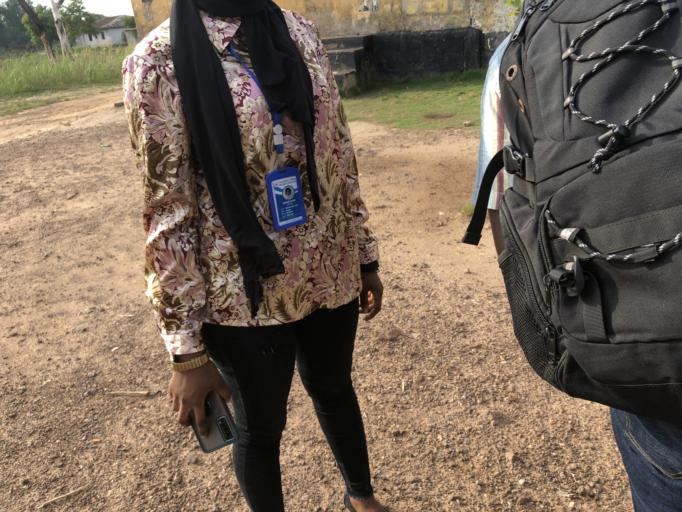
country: SL
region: Northern Province
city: Yonibana
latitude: 8.4596
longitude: -12.2021
